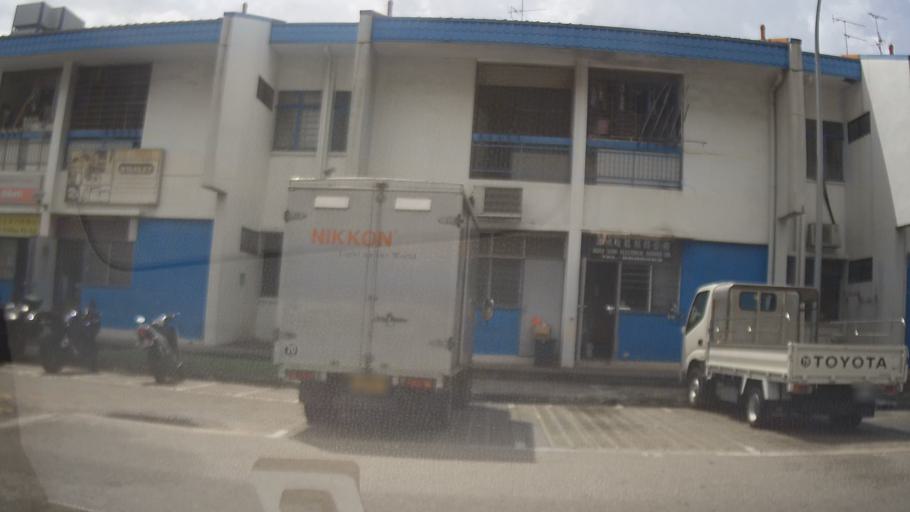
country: MY
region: Johor
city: Johor Bahru
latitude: 1.4364
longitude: 103.7543
